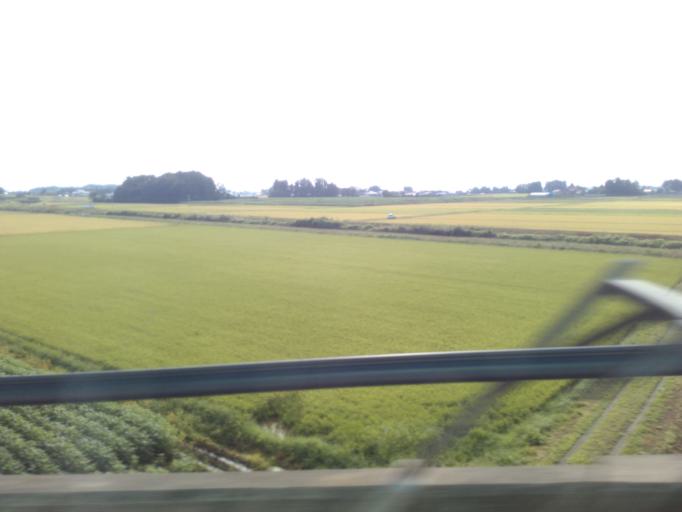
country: JP
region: Iwate
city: Ichinoseki
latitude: 38.7760
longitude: 141.0871
